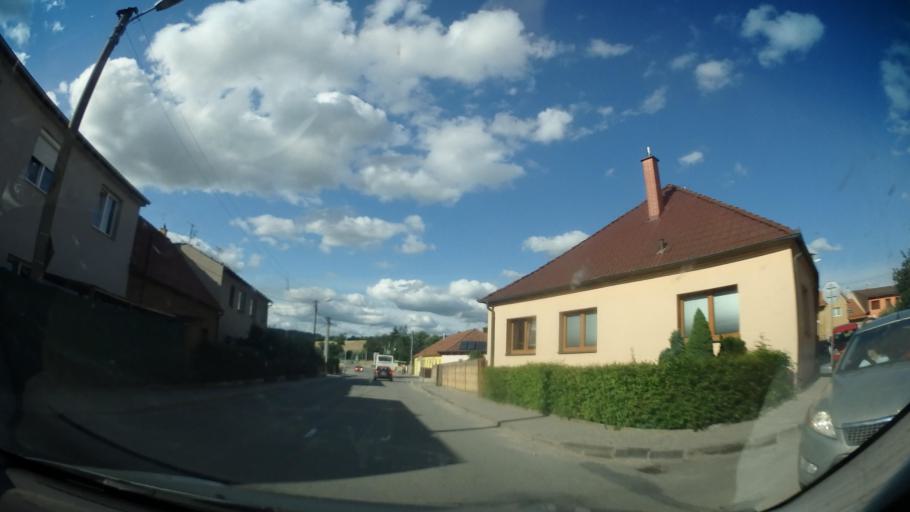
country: CZ
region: South Moravian
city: Rajecko
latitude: 49.3942
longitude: 16.6422
